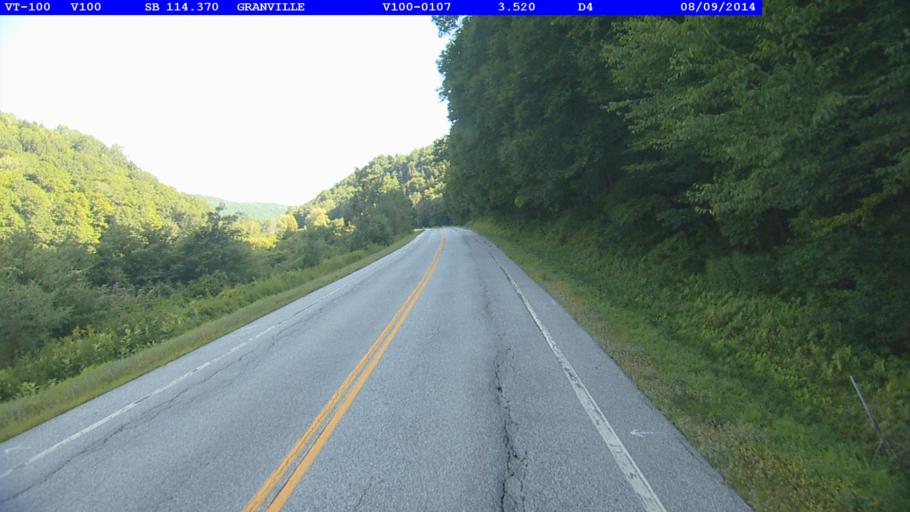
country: US
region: Vermont
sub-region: Orange County
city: Randolph
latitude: 43.9920
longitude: -72.8526
